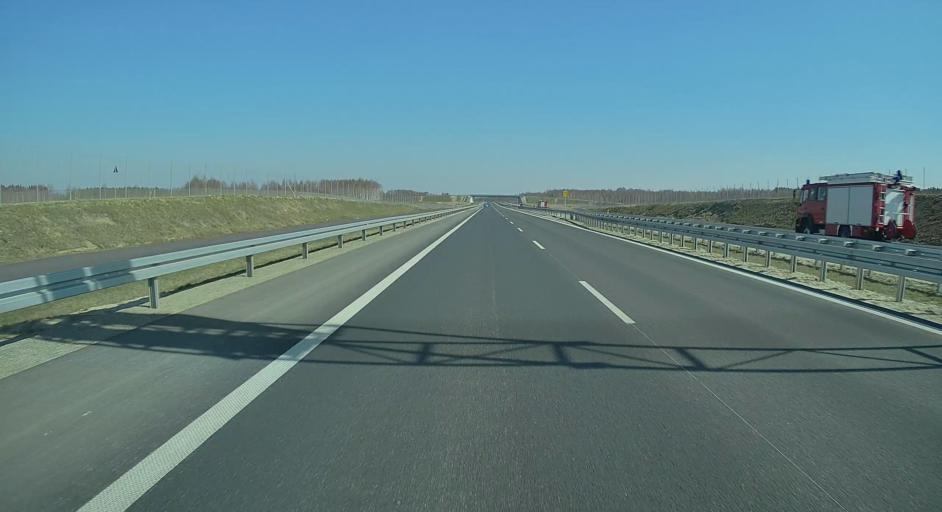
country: PL
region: Subcarpathian Voivodeship
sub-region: Powiat rzeszowski
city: Gorno
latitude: 50.3119
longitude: 22.1588
